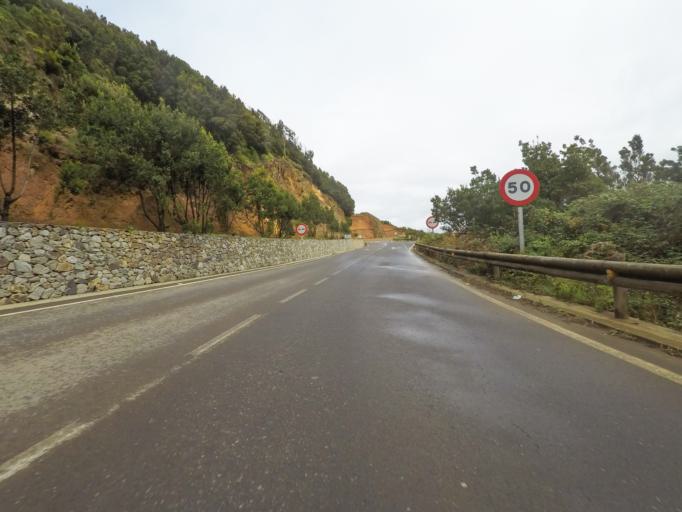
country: ES
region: Canary Islands
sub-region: Provincia de Santa Cruz de Tenerife
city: Vallehermosa
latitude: 28.1642
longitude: -17.2968
